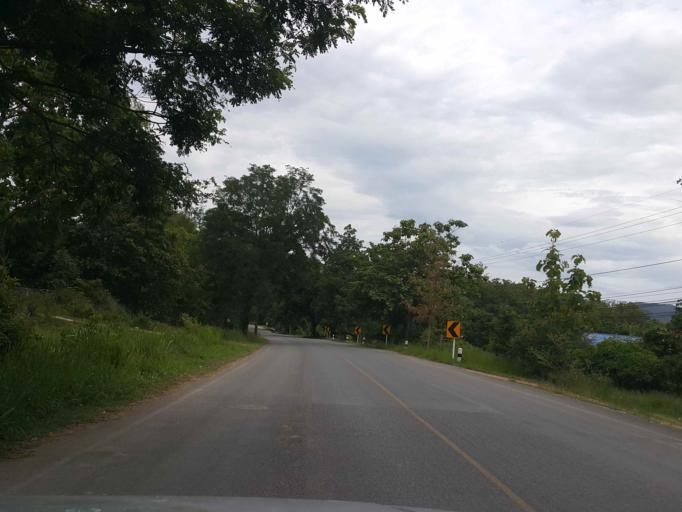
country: TH
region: Lampang
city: Thoen
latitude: 17.5923
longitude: 99.3315
